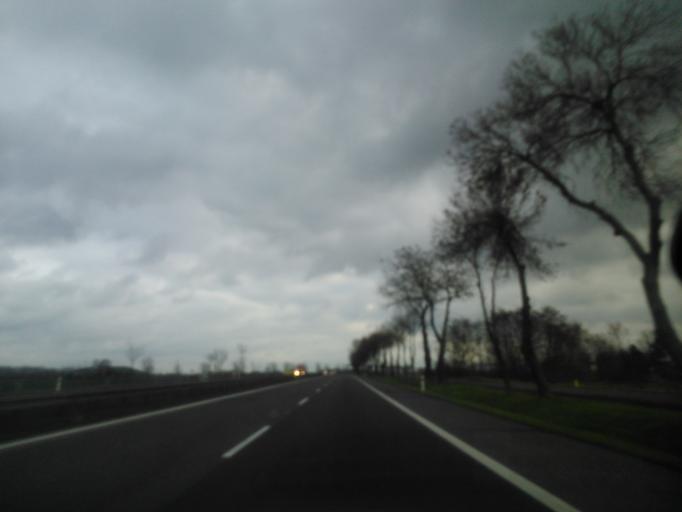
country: PL
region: Masovian Voivodeship
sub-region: Powiat plonski
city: Plonsk
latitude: 52.5940
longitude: 20.4368
